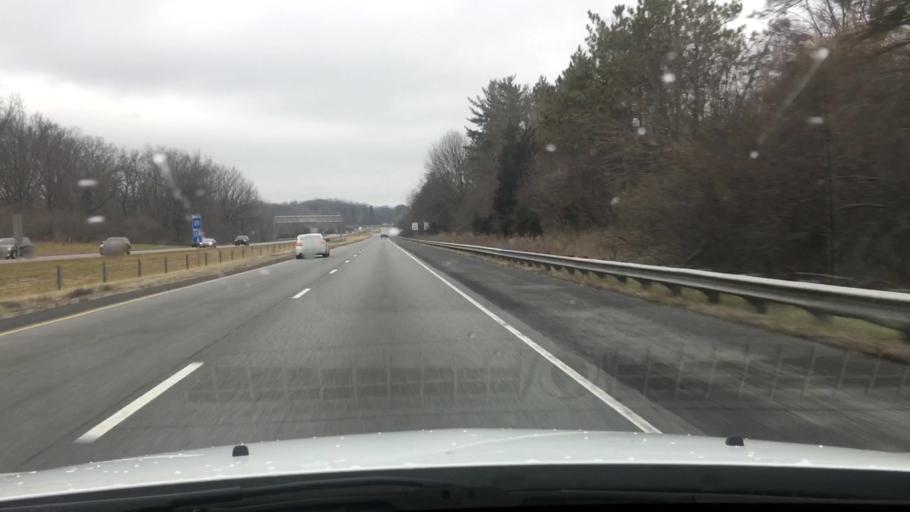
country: US
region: Indiana
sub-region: Boone County
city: Zionsville
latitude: 39.8838
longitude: -86.2967
